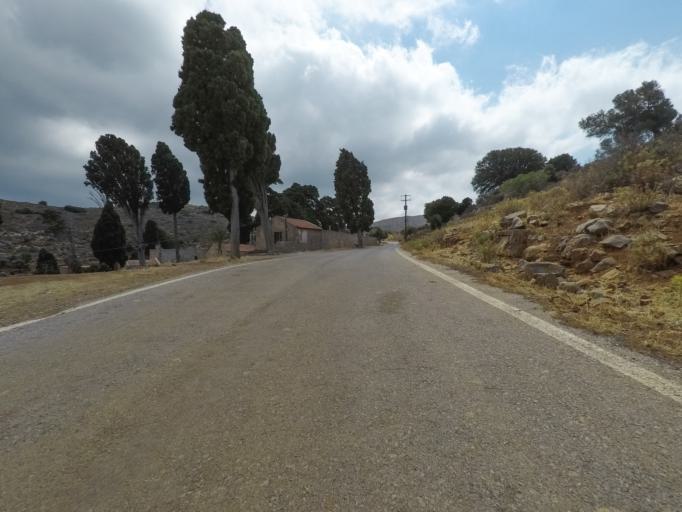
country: GR
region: Crete
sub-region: Nomos Lasithiou
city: Elounda
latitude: 35.3025
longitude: 25.6807
